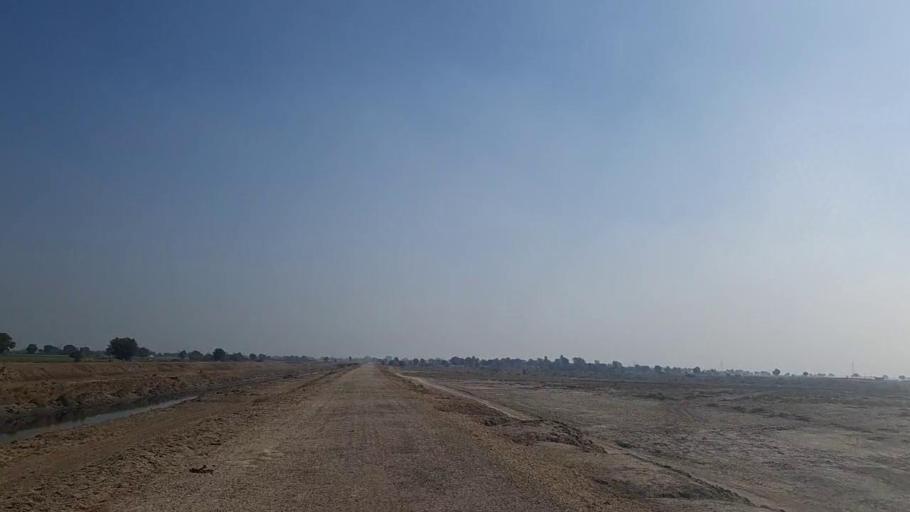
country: PK
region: Sindh
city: Shahpur Chakar
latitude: 26.1873
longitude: 68.5585
